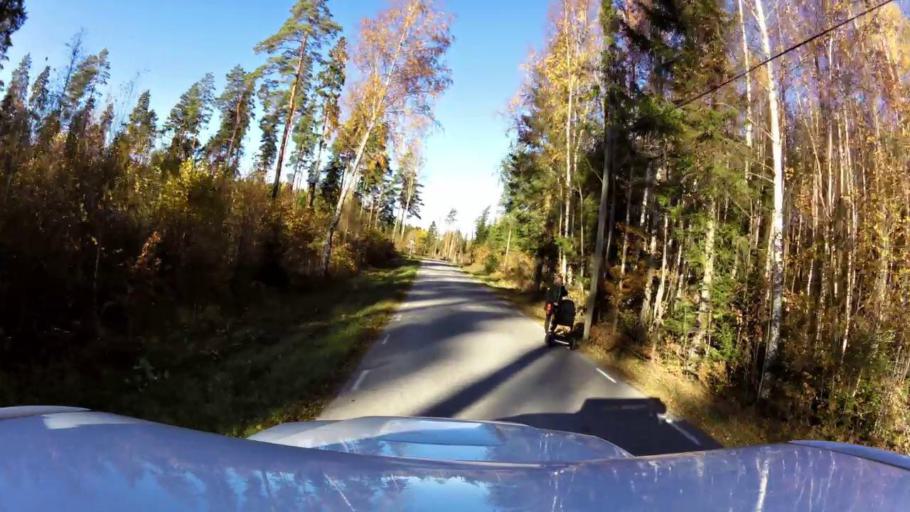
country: SE
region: OEstergoetland
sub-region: Linkopings Kommun
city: Ljungsbro
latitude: 58.5240
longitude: 15.4886
